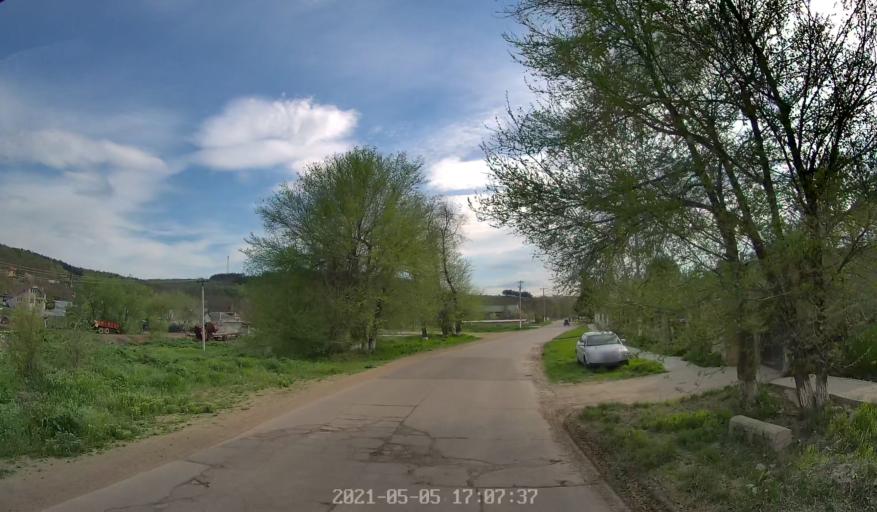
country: MD
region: Chisinau
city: Vadul lui Voda
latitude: 47.0115
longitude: 29.1333
